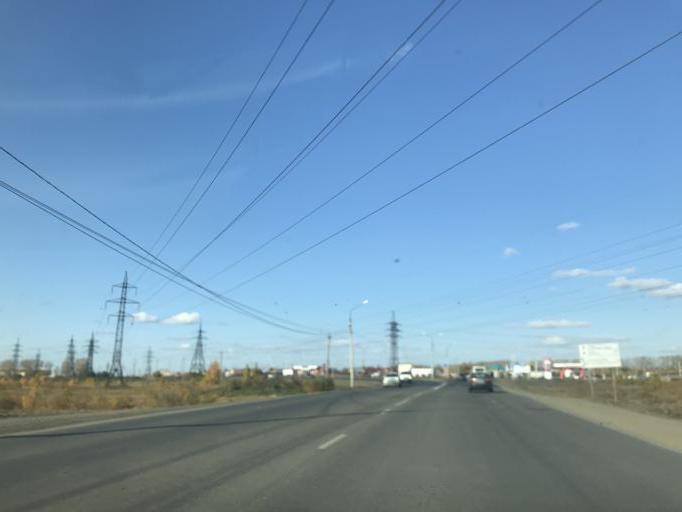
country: RU
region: Chelyabinsk
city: Roshchino
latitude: 55.2276
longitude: 61.2876
